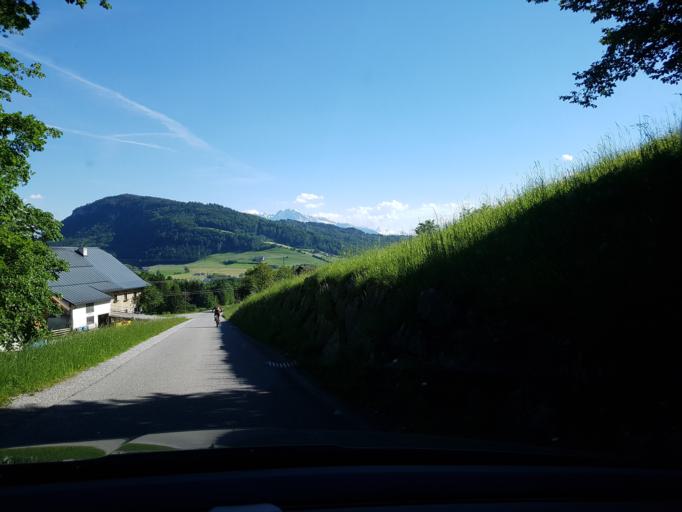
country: AT
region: Salzburg
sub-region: Politischer Bezirk Salzburg-Umgebung
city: Koppl
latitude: 47.7831
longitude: 13.1233
